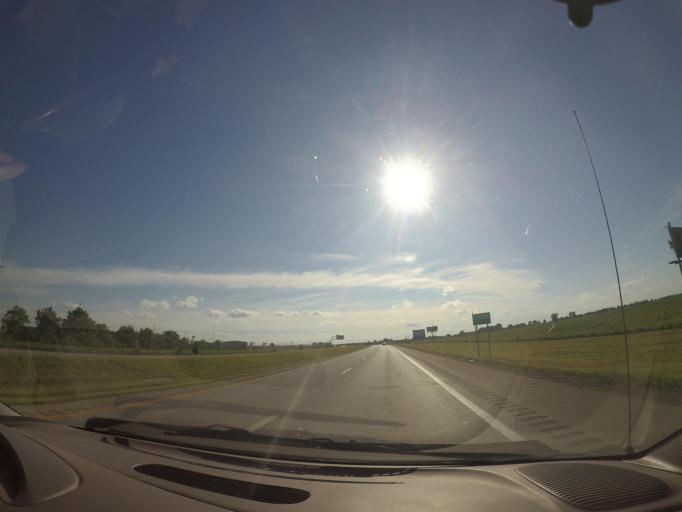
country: US
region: Ohio
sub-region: Henry County
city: Napoleon
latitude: 41.4170
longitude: -84.0860
